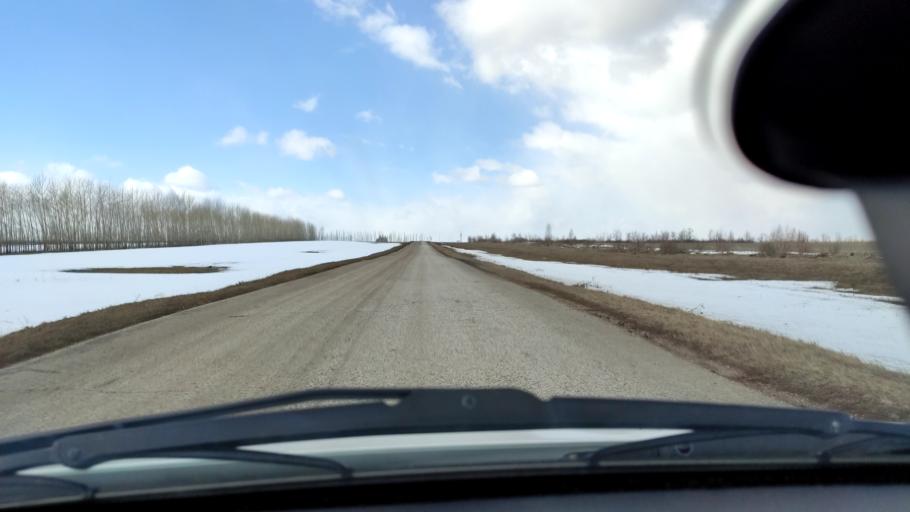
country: RU
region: Bashkortostan
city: Tolbazy
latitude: 54.1708
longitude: 55.9114
